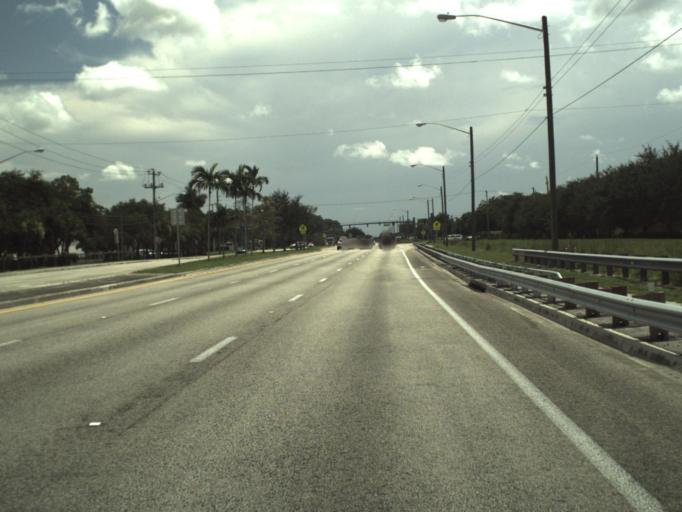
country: US
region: Florida
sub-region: Palm Beach County
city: Wellington
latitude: 26.6171
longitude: -80.1923
